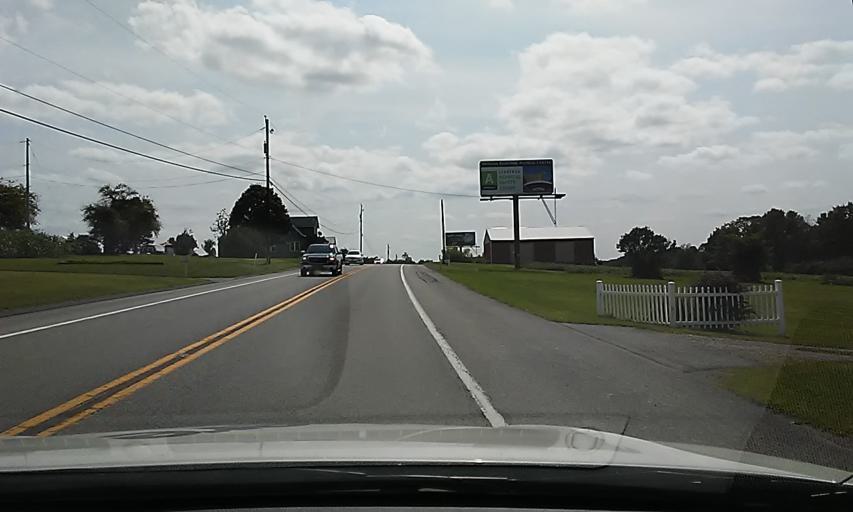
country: US
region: Pennsylvania
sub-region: Jefferson County
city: Punxsutawney
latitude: 40.8616
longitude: -79.0213
